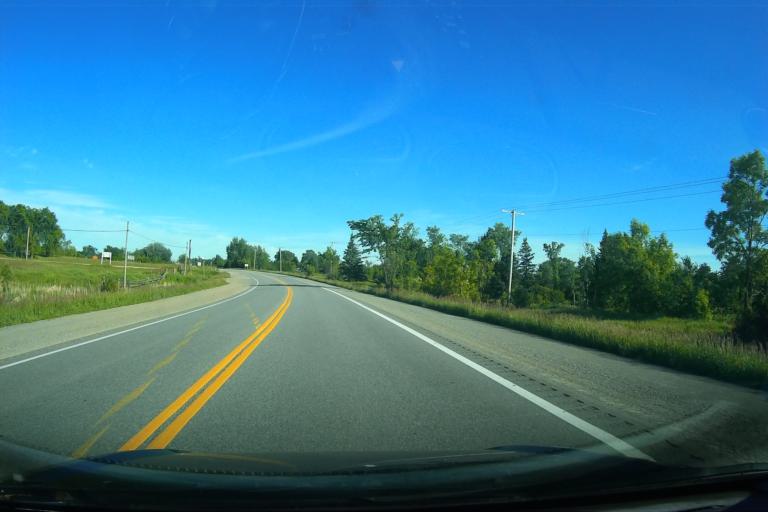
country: CA
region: Quebec
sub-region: Outaouais
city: Fort-Coulonge
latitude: 45.6411
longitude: -76.8997
